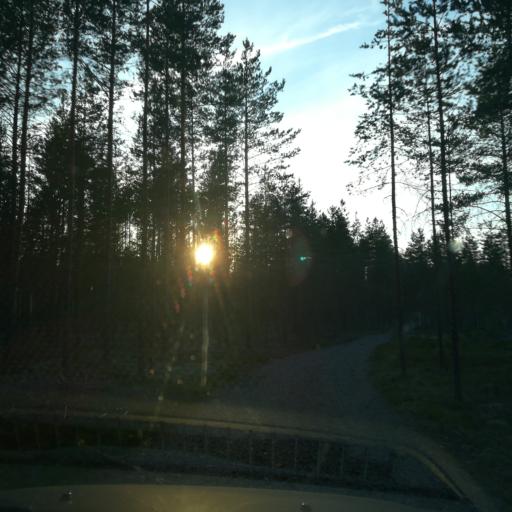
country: FI
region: Southern Savonia
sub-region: Mikkeli
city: Puumala
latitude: 61.4342
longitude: 28.4623
